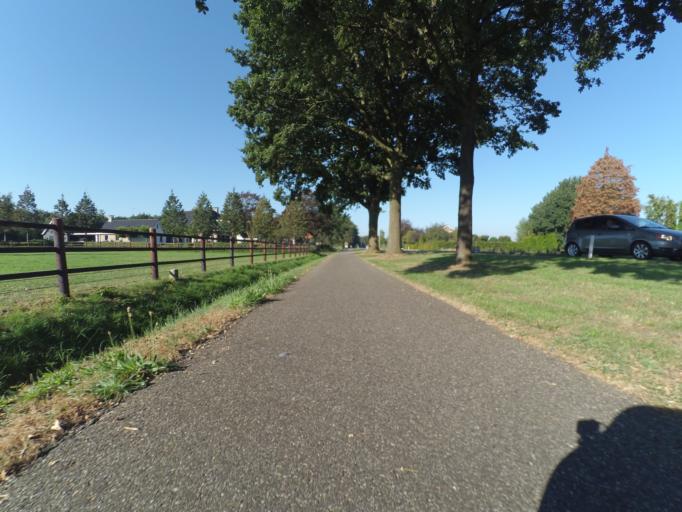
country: NL
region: Gelderland
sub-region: Gemeente Putten
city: Putten
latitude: 52.2557
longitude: 5.5854
